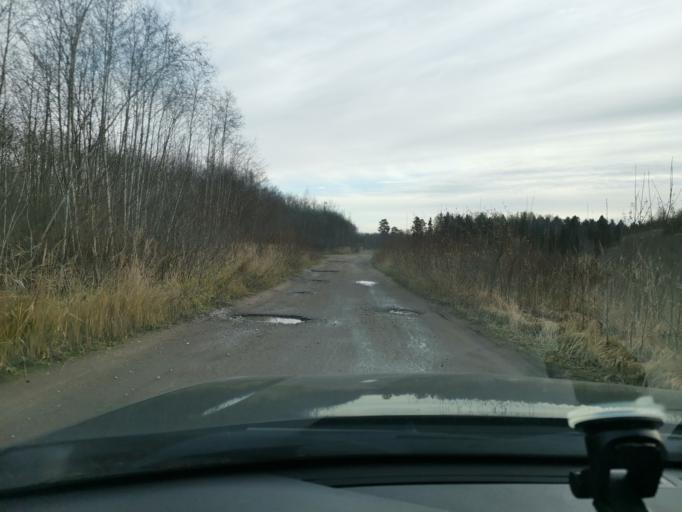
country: EE
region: Ida-Virumaa
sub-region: Sillamaee linn
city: Sillamae
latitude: 59.2598
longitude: 27.9109
